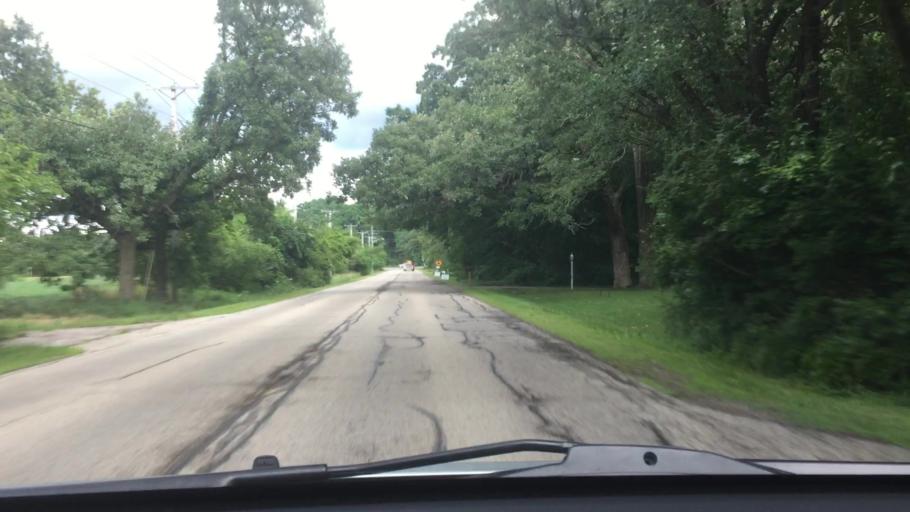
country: US
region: Illinois
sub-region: McHenry County
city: Prairie Grove
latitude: 42.2848
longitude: -88.2906
